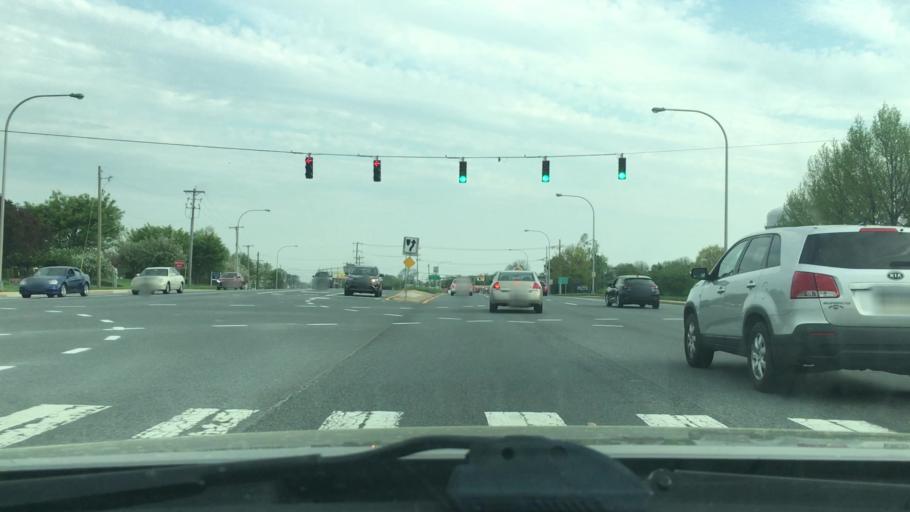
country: US
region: Delaware
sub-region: New Castle County
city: Greenville
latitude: 39.8135
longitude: -75.5499
